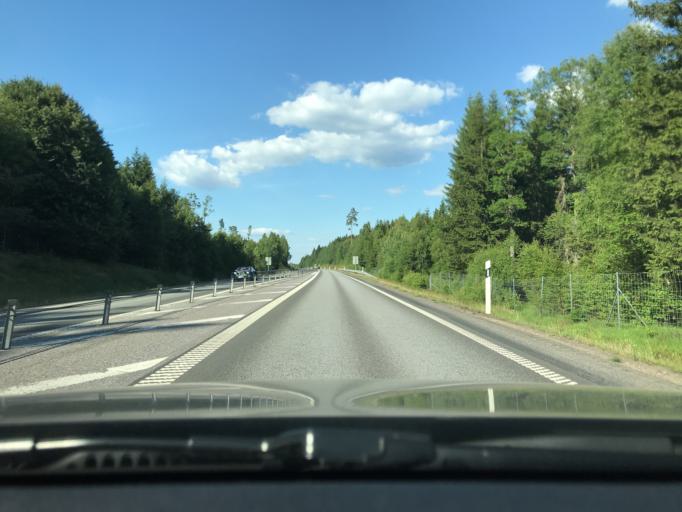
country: SE
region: Kronoberg
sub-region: Almhults Kommun
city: AElmhult
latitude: 56.4588
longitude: 14.0944
